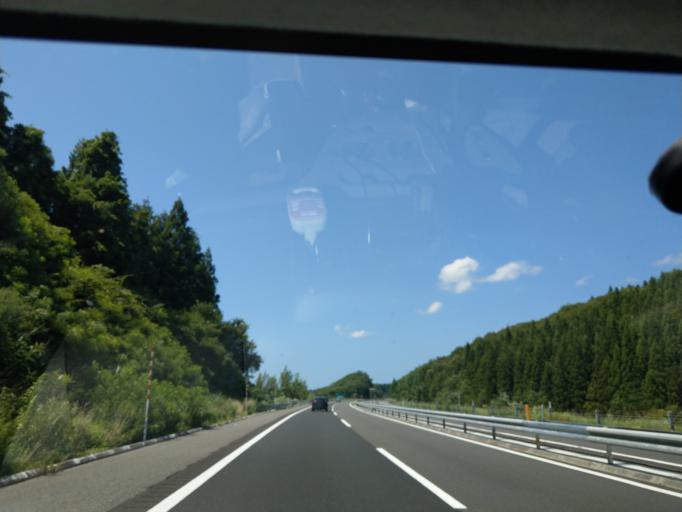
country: JP
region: Akita
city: Akita
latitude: 39.6254
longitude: 140.2338
